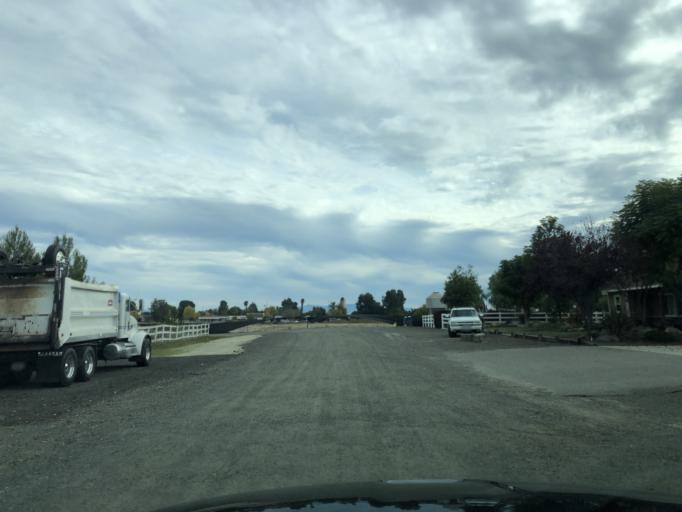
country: US
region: California
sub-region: Riverside County
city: Wildomar
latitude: 33.6073
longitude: -117.2826
